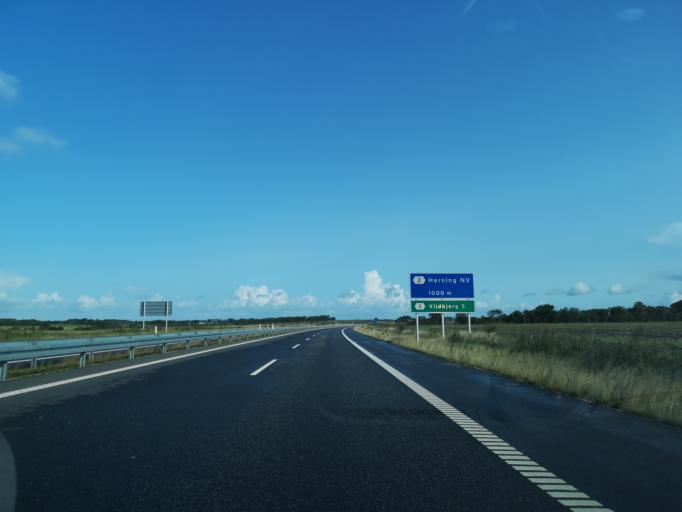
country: DK
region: Central Jutland
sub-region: Herning Kommune
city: Snejbjerg
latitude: 56.1397
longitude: 8.8698
